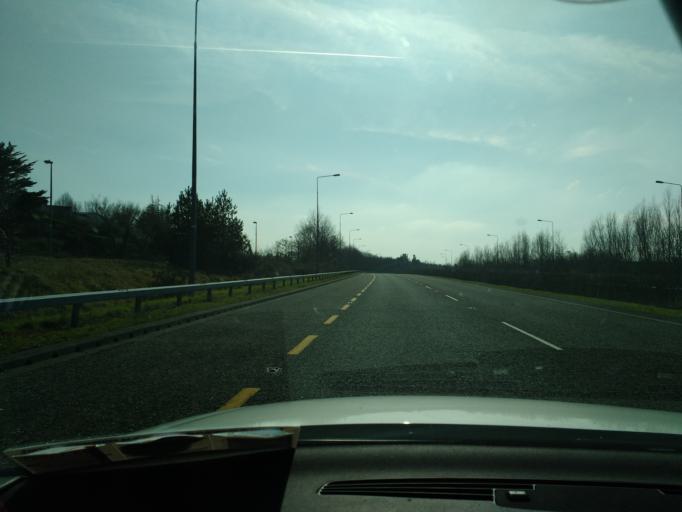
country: IE
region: Munster
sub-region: An Clar
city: Shannon
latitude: 52.7085
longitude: -8.8888
